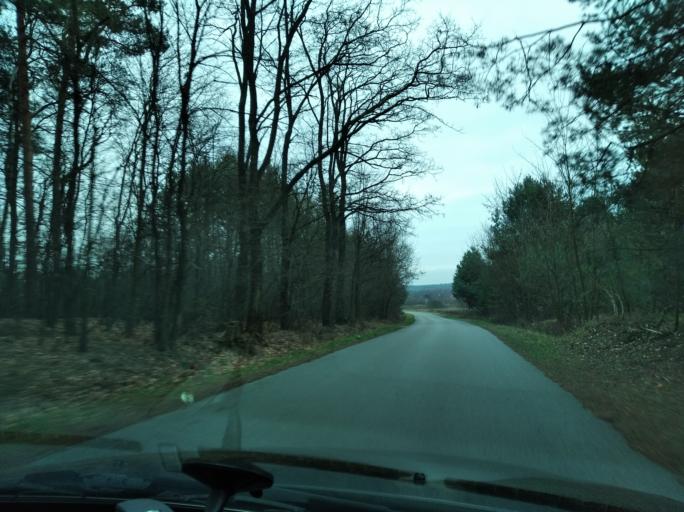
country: PL
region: Subcarpathian Voivodeship
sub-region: Powiat lancucki
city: Brzoza Stadnicka
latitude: 50.2031
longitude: 22.2774
